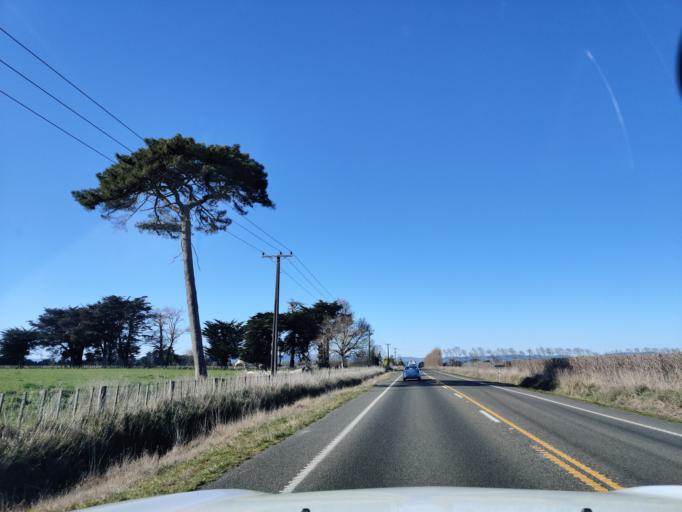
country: NZ
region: Manawatu-Wanganui
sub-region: Palmerston North City
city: Palmerston North
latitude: -40.2973
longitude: 175.5754
